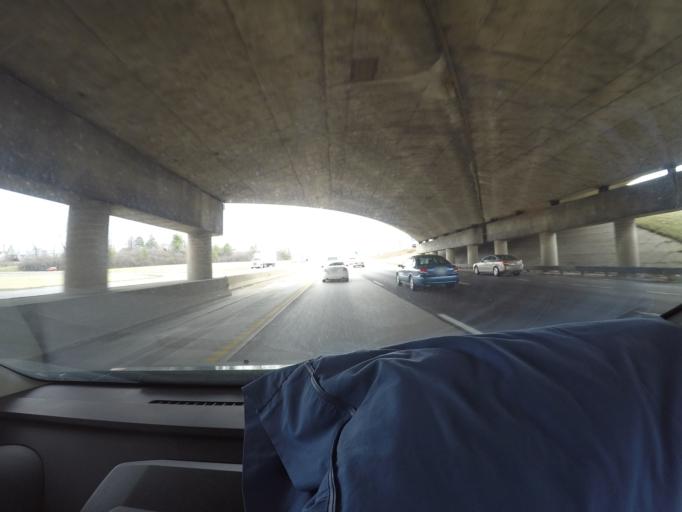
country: US
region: Missouri
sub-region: Saint Louis County
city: Bridgeton
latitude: 38.7438
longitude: -90.4124
